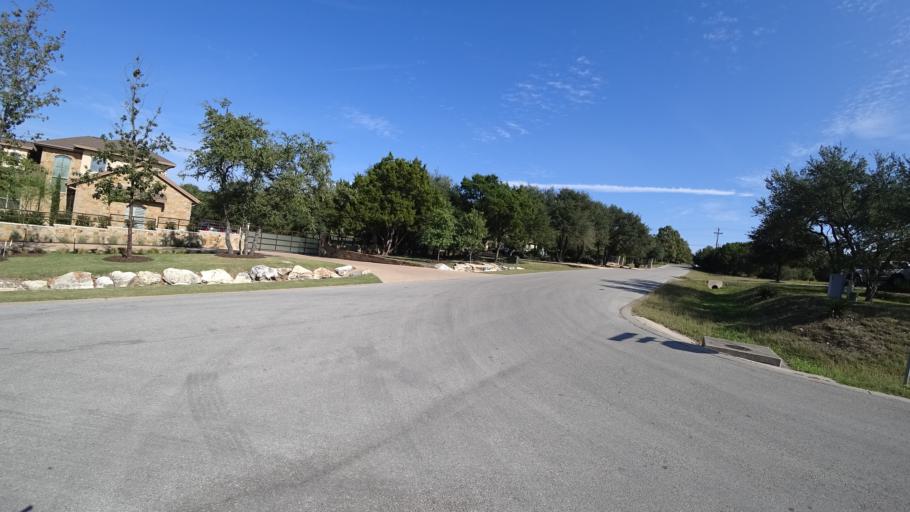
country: US
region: Texas
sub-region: Travis County
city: Barton Creek
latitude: 30.2230
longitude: -97.9121
